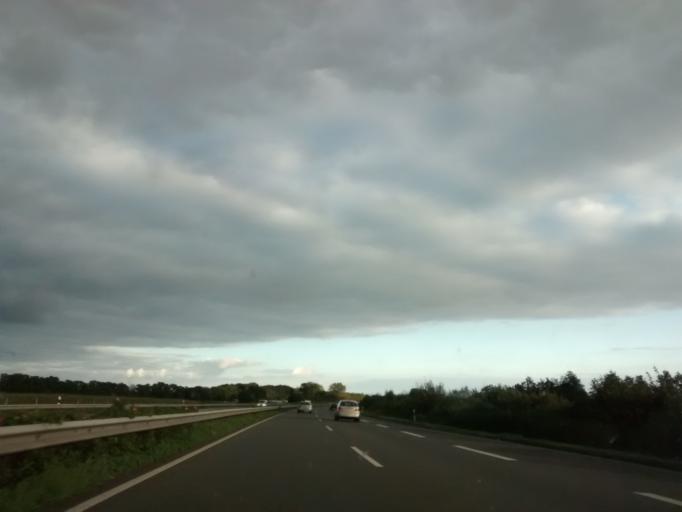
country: DE
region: Lower Saxony
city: Salzbergen
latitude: 52.3408
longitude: 7.4021
